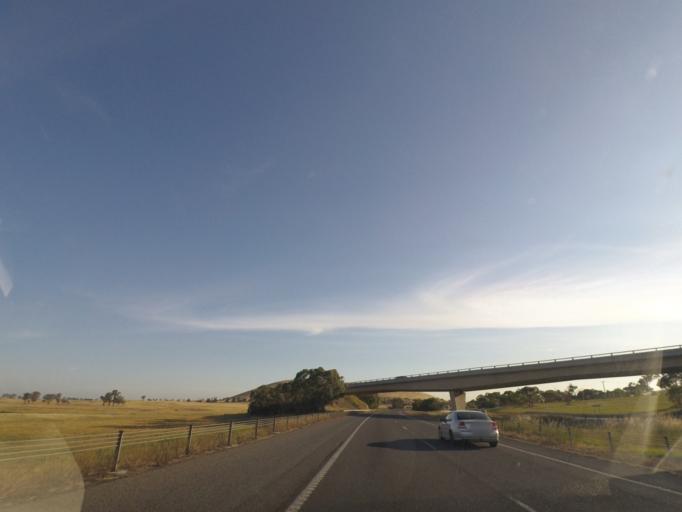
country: AU
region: Victoria
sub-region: Whittlesea
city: Whittlesea
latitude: -37.4456
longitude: 144.9815
